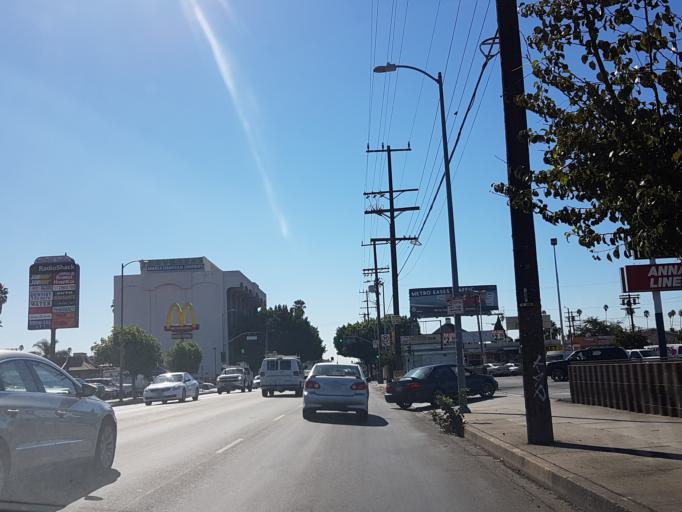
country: US
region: California
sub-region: Los Angeles County
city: Hollywood
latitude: 34.0426
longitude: -118.3091
